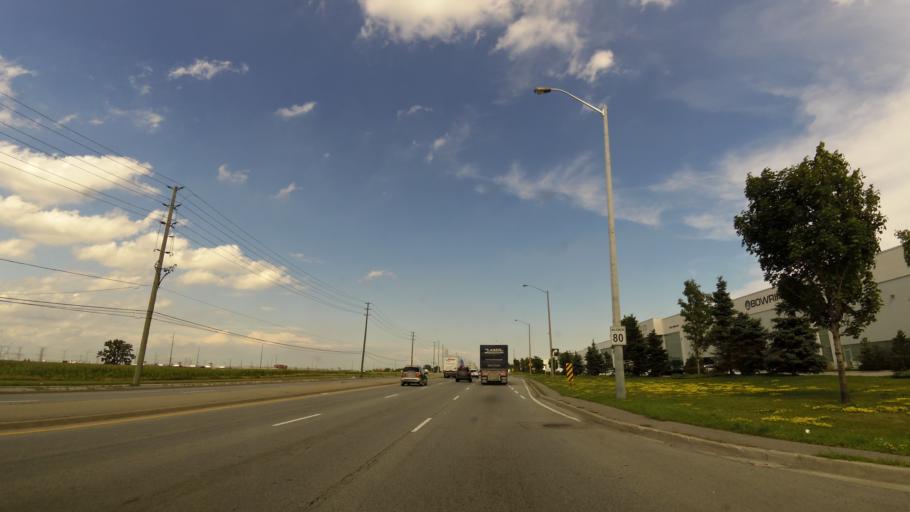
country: CA
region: Ontario
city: Brampton
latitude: 43.7302
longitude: -79.6616
